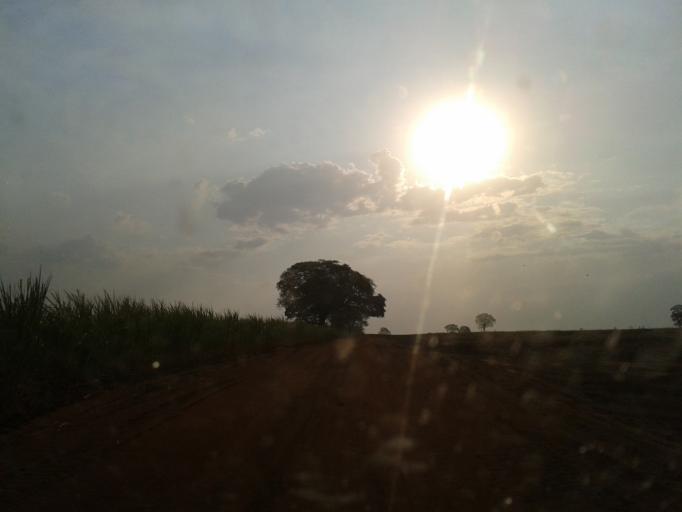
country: BR
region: Minas Gerais
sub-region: Capinopolis
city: Capinopolis
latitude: -18.7567
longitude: -49.6904
